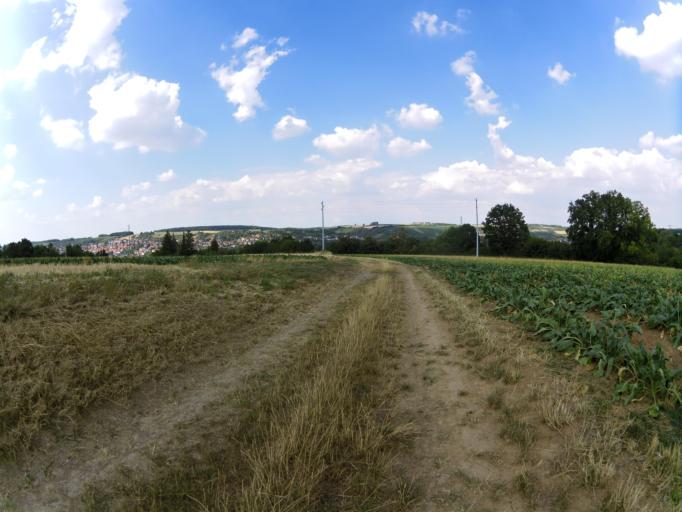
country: DE
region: Bavaria
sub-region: Regierungsbezirk Unterfranken
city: Ochsenfurt
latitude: 49.6580
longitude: 10.0678
